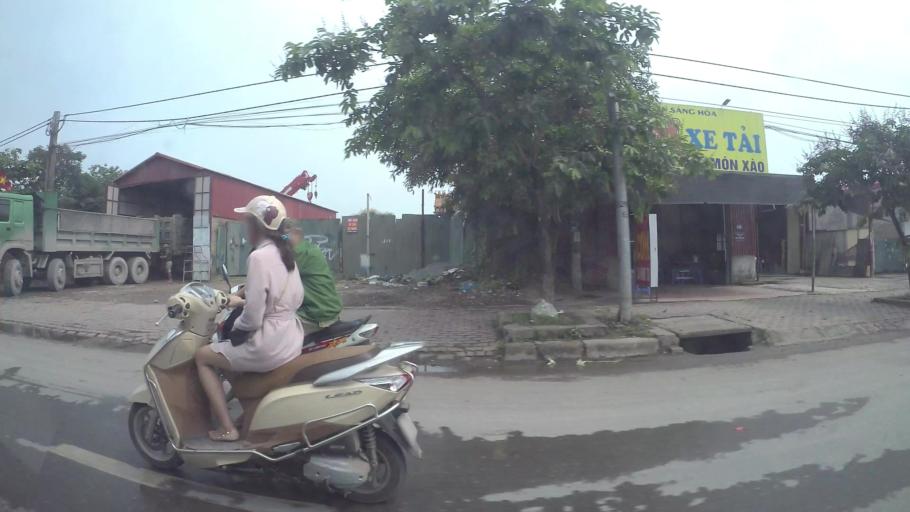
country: VN
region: Ha Noi
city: Van Dien
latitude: 20.9644
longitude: 105.8602
